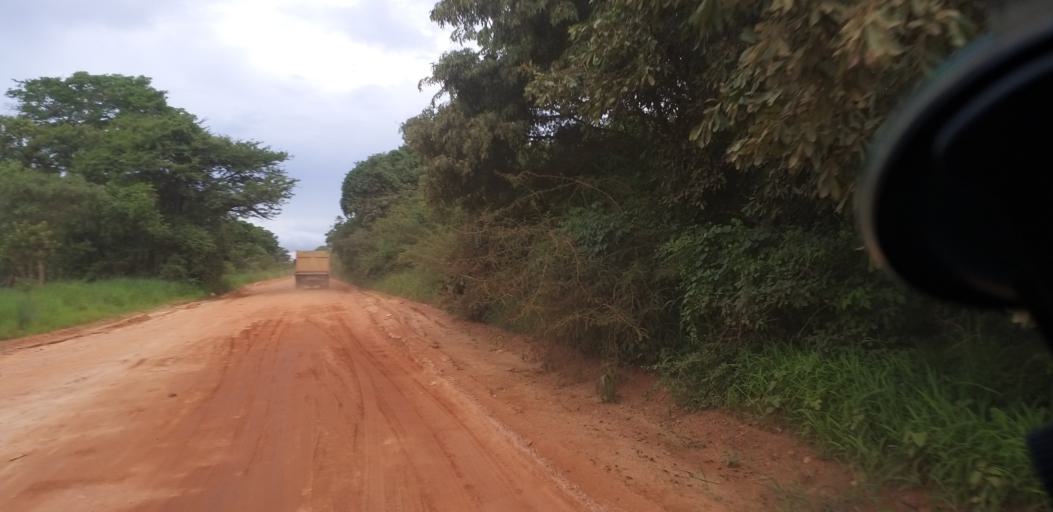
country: ZM
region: Lusaka
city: Lusaka
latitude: -15.1987
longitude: 28.4403
